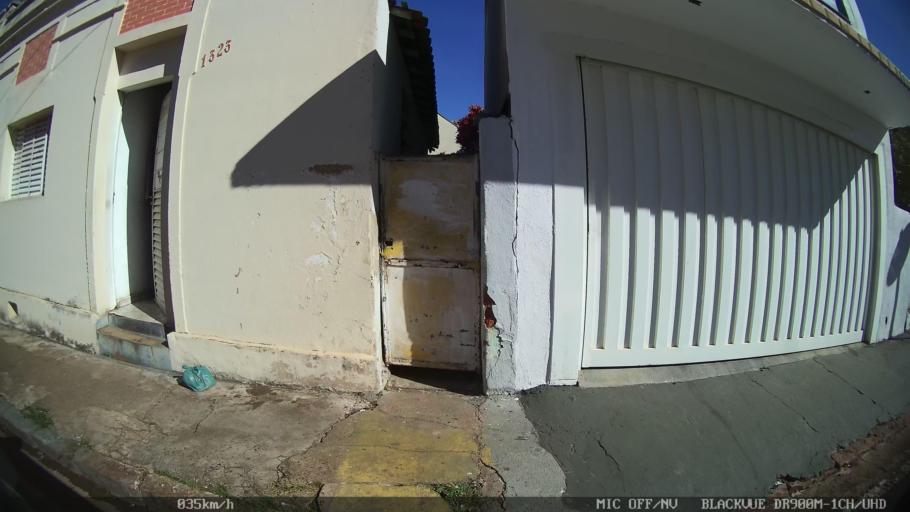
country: BR
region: Sao Paulo
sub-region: Franca
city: Franca
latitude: -20.5422
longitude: -47.4002
